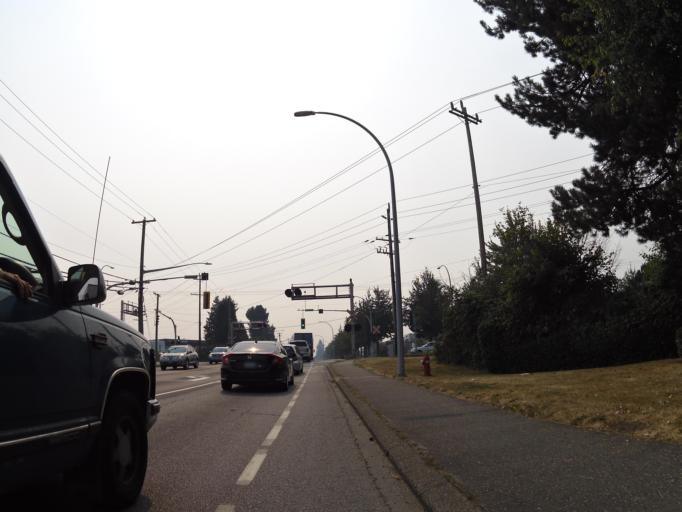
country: CA
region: British Columbia
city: Surrey
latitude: 49.1414
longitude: -122.8568
